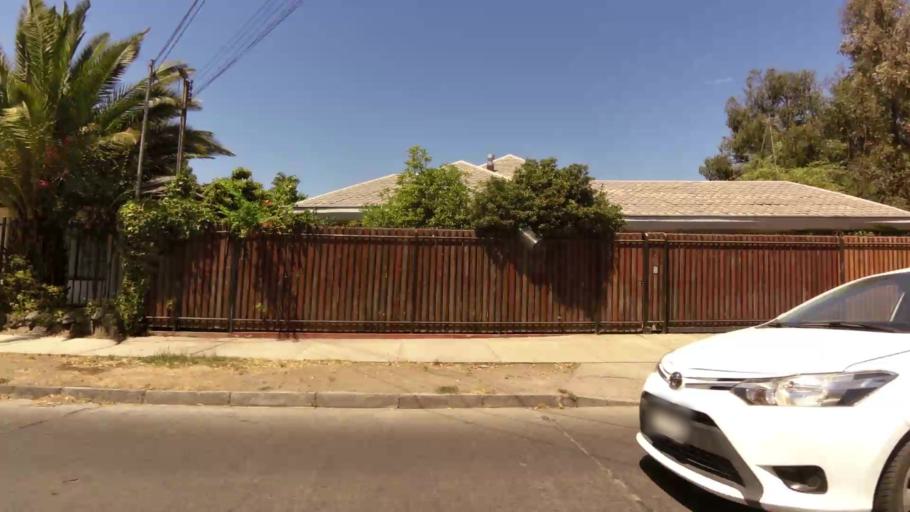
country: CL
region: Maule
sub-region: Provincia de Curico
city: Curico
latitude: -34.9842
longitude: -71.2218
